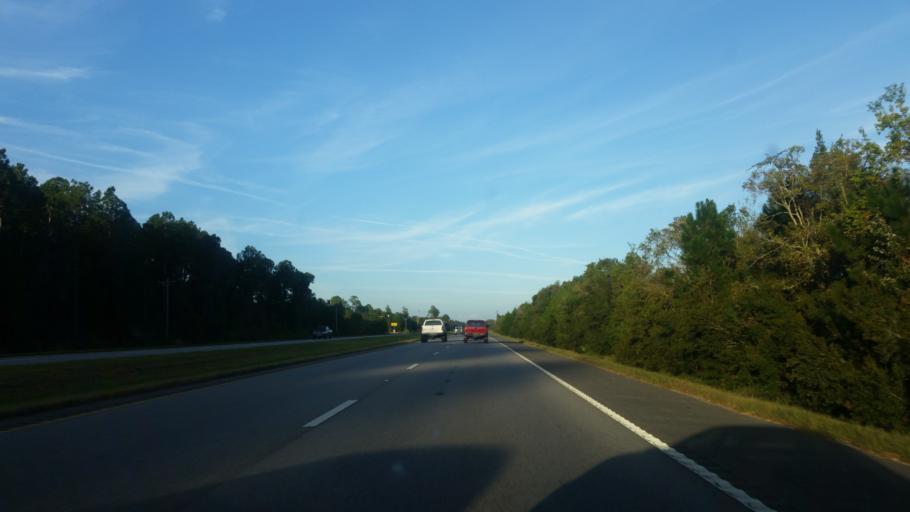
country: US
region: Mississippi
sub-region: Jackson County
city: Moss Point
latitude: 30.4145
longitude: -88.4693
